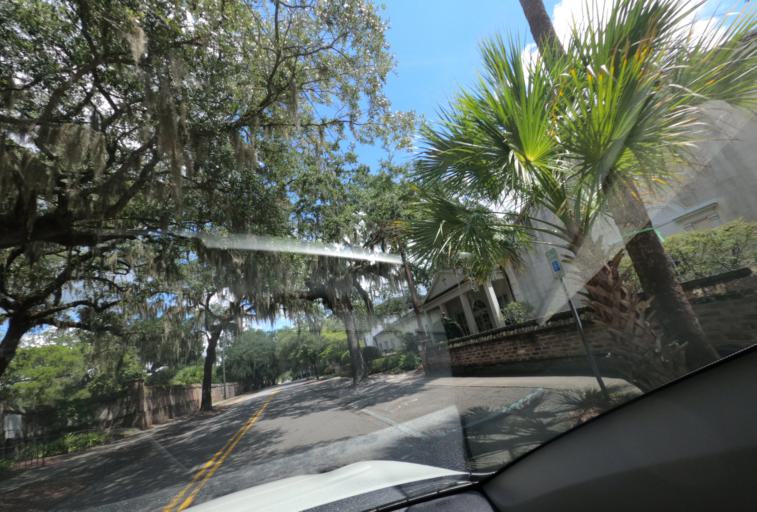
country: US
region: South Carolina
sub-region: Beaufort County
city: Beaufort
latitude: 32.4337
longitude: -80.6740
